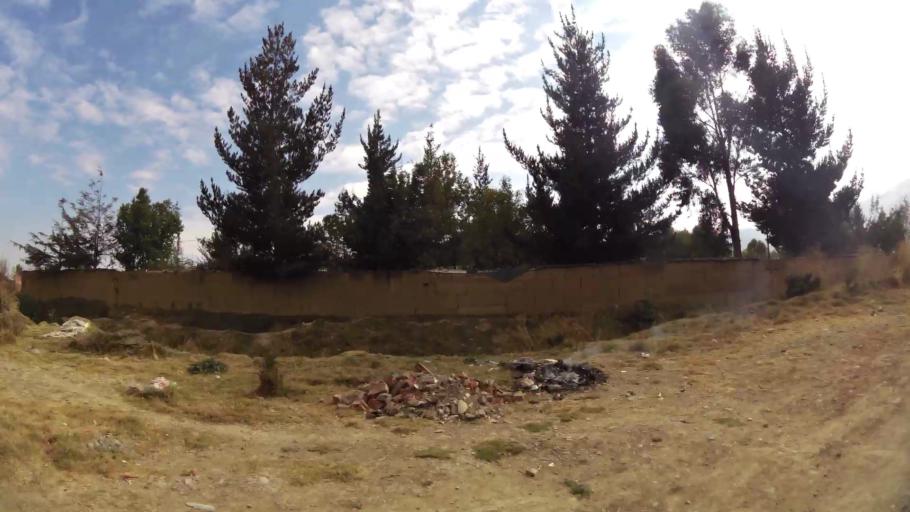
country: PE
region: Junin
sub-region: Provincia de Huancayo
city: Huancayo
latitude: -12.0557
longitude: -75.1957
